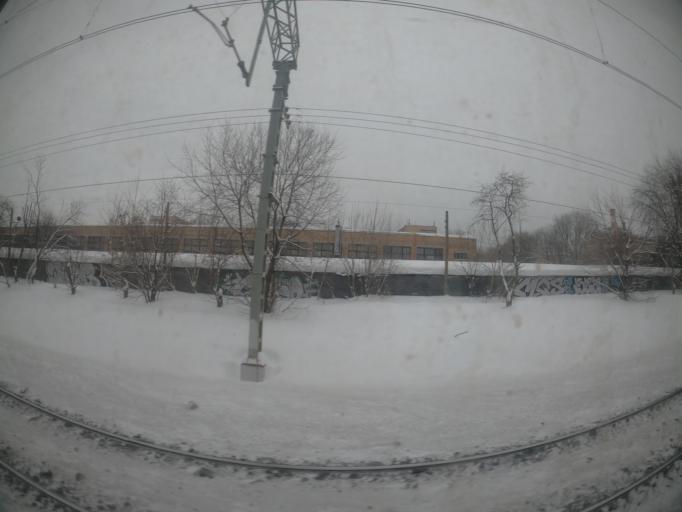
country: RU
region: Moscow
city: Kotlovka
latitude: 55.6756
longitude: 37.6225
